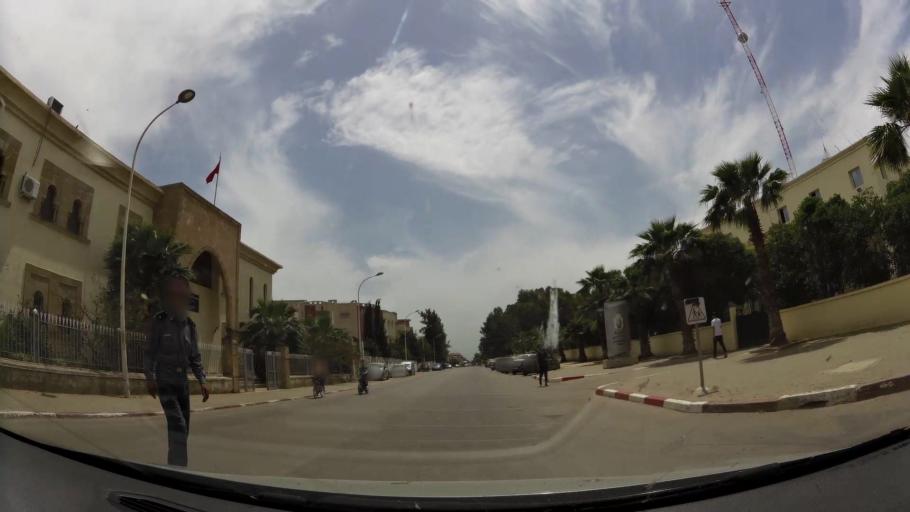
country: MA
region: Rabat-Sale-Zemmour-Zaer
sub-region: Khemisset
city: Khemisset
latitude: 33.8187
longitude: -6.0694
